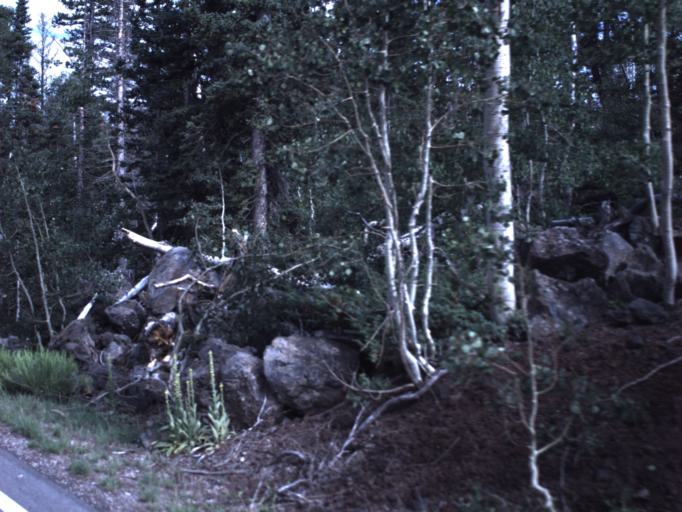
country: US
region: Utah
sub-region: Iron County
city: Parowan
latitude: 37.5229
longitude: -112.7384
